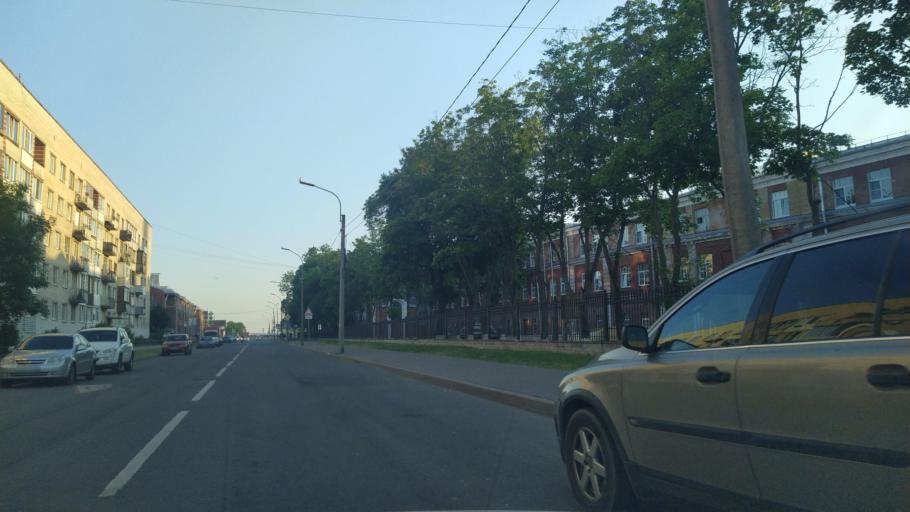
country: RU
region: St.-Petersburg
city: Kronshtadt
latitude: 59.9943
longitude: 29.7567
